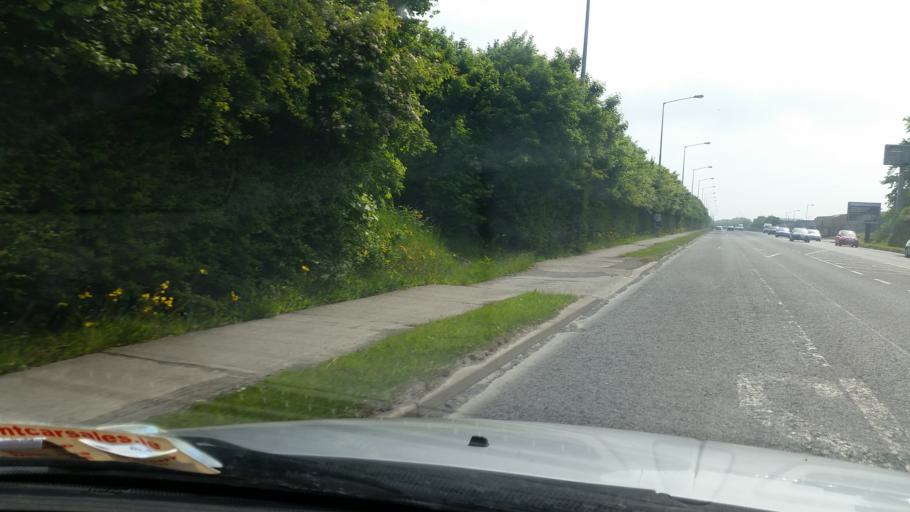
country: IE
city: Bonnybrook
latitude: 53.4081
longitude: -6.2053
